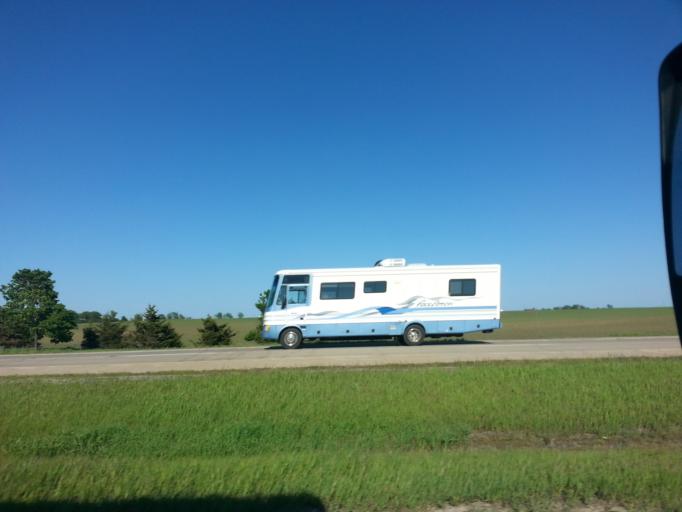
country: US
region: Illinois
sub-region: LaSalle County
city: Oglesby
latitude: 41.1980
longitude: -89.0767
